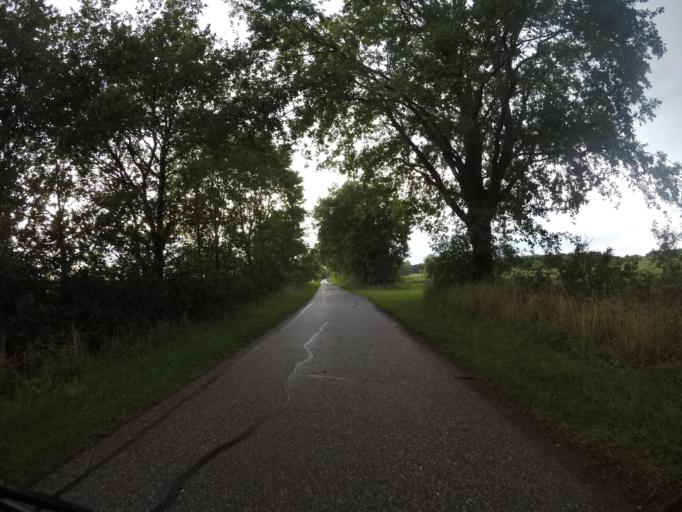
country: DE
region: Lower Saxony
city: Neu Darchau
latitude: 53.2656
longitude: 10.9026
